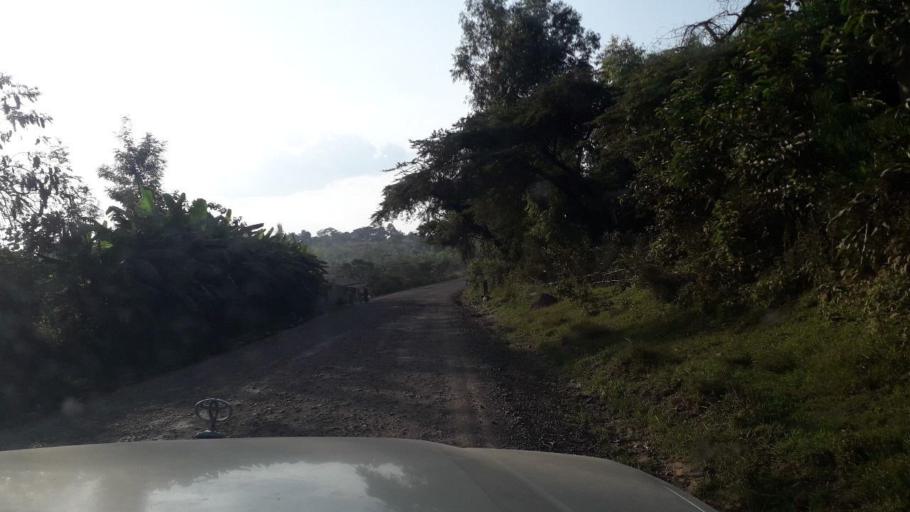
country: ET
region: Oromiya
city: Jima
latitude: 7.5928
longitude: 36.8533
